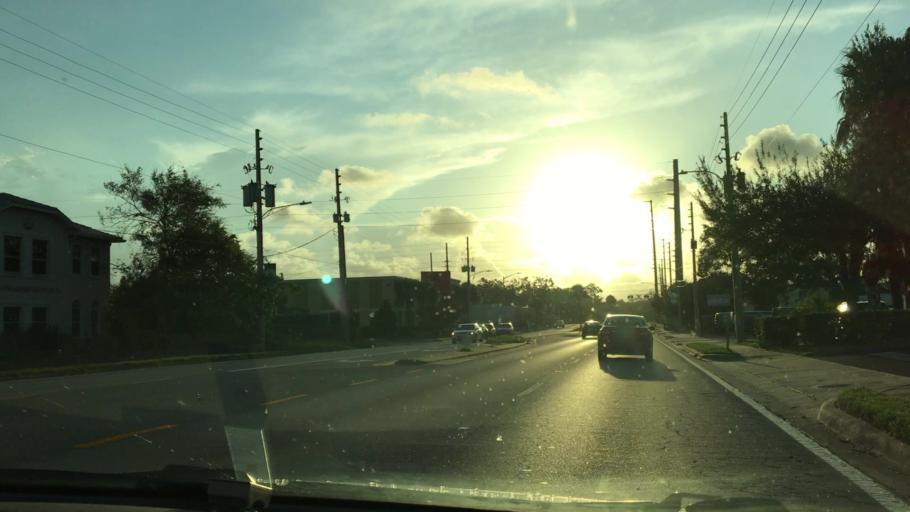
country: US
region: Florida
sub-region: Orange County
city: Holden Heights
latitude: 28.5130
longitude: -81.3783
